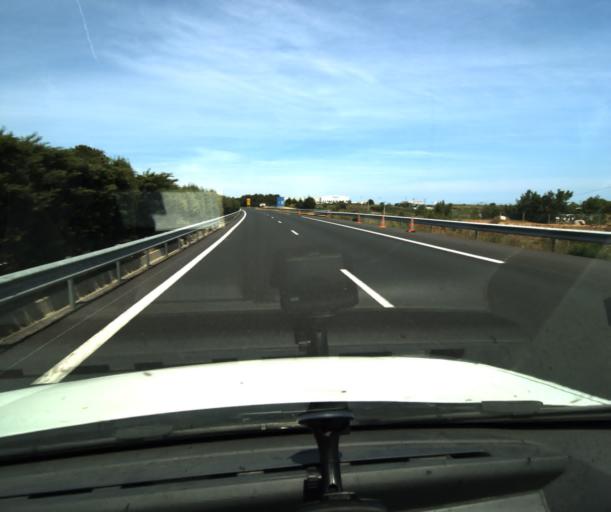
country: FR
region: Languedoc-Roussillon
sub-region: Departement des Pyrenees-Orientales
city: Pia
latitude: 42.7463
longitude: 2.8916
